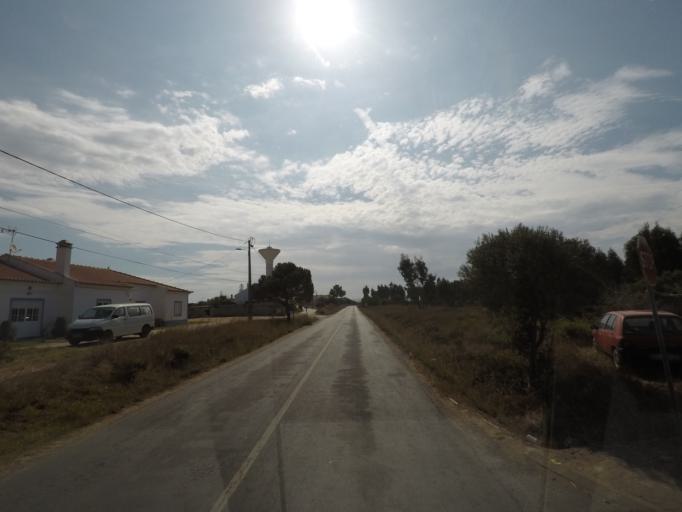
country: PT
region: Beja
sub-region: Odemira
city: Sao Teotonio
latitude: 37.4756
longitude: -8.7603
